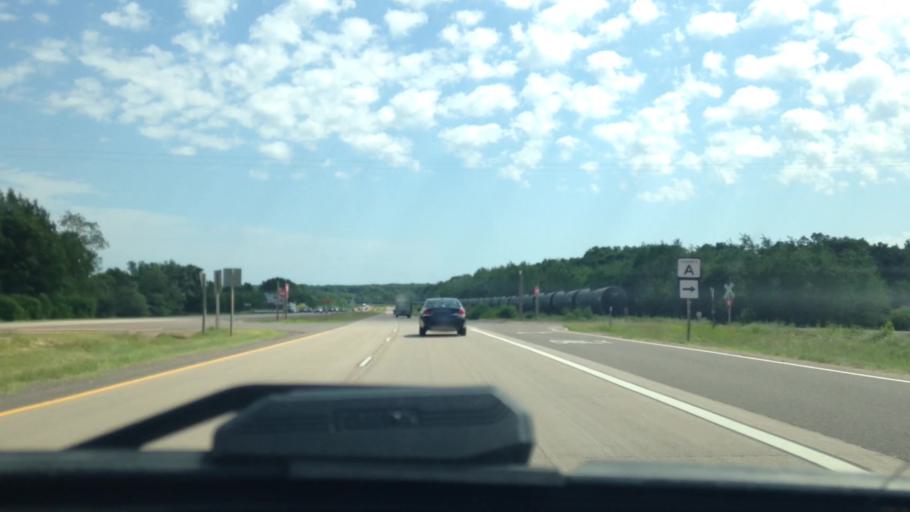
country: US
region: Wisconsin
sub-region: Washburn County
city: Spooner
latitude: 45.8585
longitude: -91.8483
